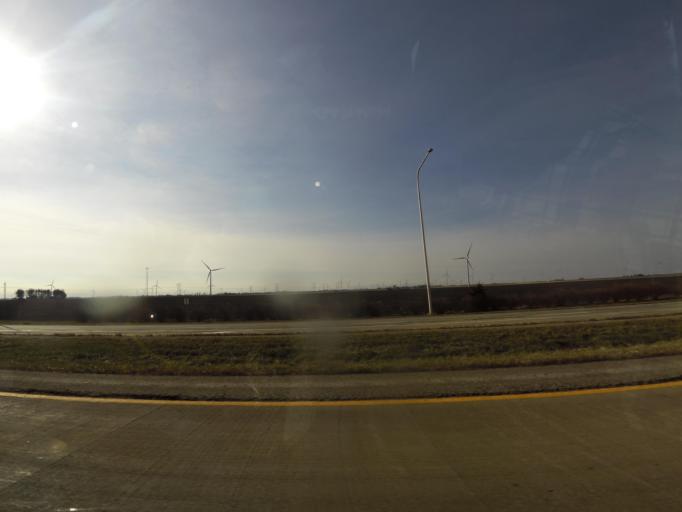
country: US
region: Illinois
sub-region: Macon County
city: Maroa
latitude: 40.0288
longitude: -88.9589
